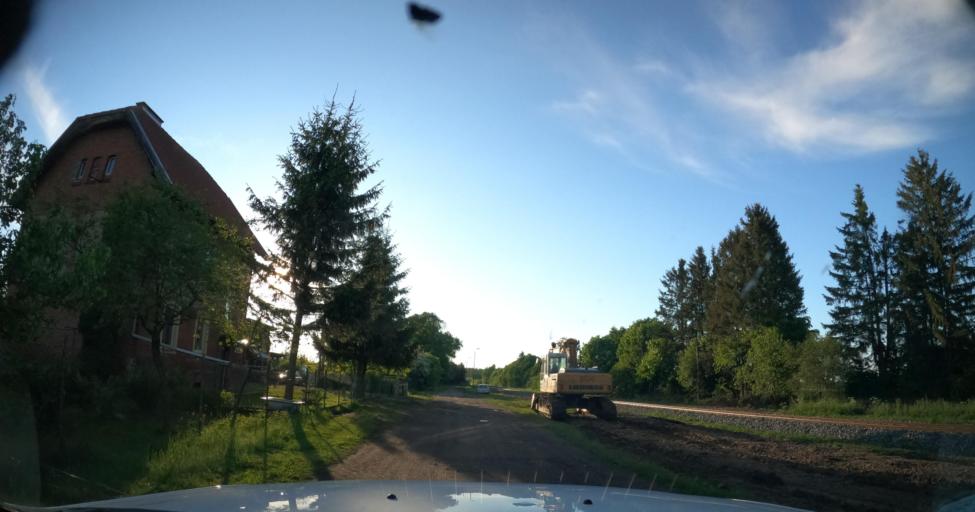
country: PL
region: Warmian-Masurian Voivodeship
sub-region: Powiat braniewski
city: Pieniezno
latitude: 54.1831
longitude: 20.1321
